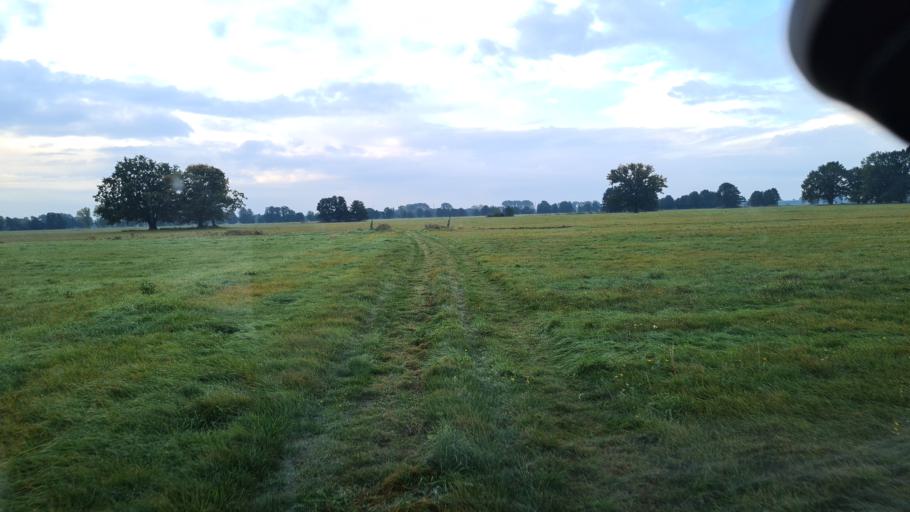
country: DE
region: Brandenburg
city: Schonewalde
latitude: 51.6773
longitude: 13.5710
